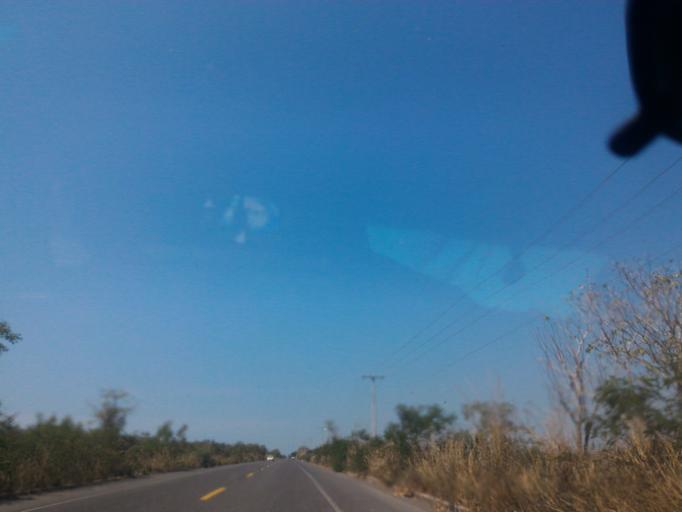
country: MX
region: Michoacan
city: Coahuayana Viejo
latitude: 18.7762
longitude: -103.7521
